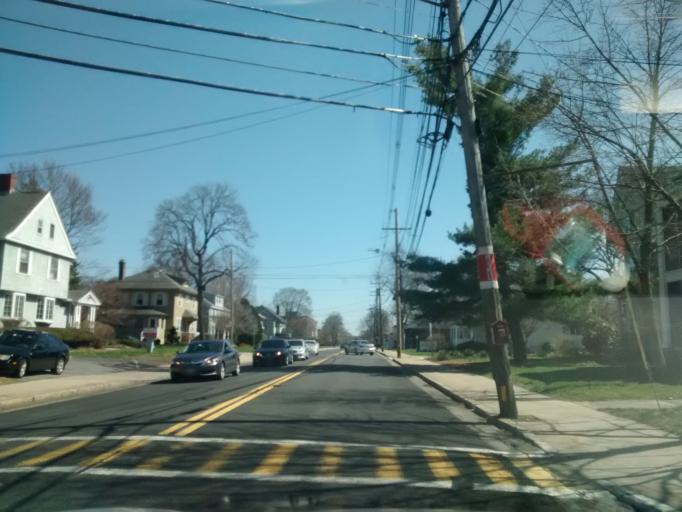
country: US
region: Massachusetts
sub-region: Middlesex County
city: Framingham
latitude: 42.2888
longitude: -71.4244
